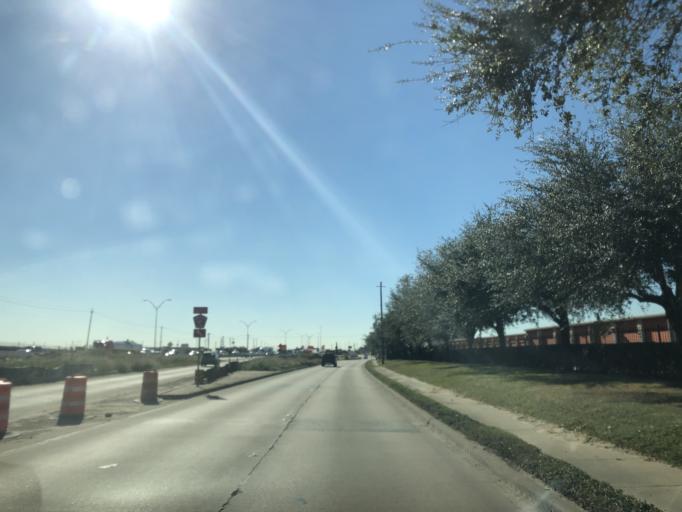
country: US
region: Texas
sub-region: Harris County
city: Deer Park
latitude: 29.6641
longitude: -95.1562
